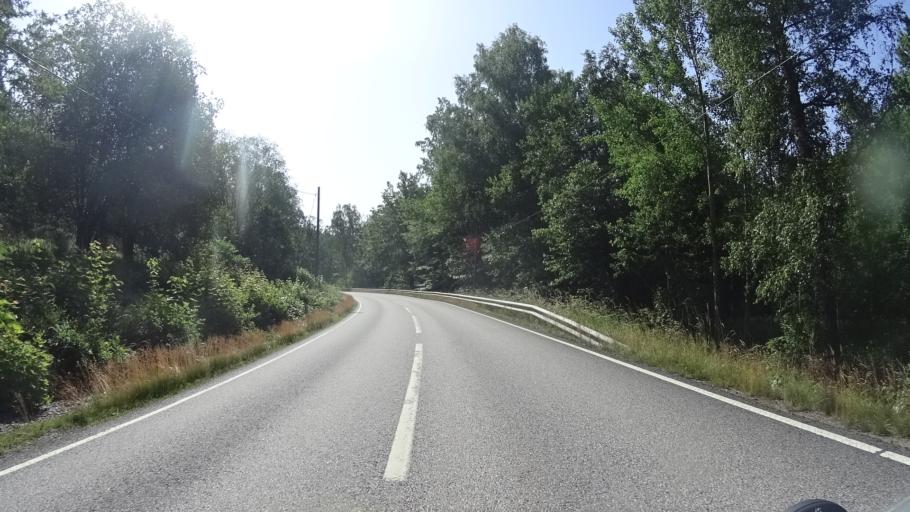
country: SE
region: Kalmar
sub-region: Vasterviks Kommun
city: Overum
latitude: 58.0205
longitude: 16.2441
